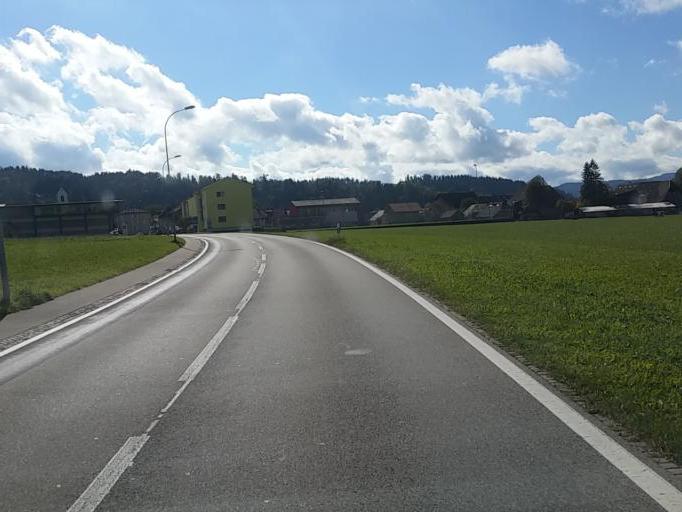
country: CH
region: Bern
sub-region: Emmental District
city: Sumiswald
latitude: 47.0322
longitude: 7.7419
